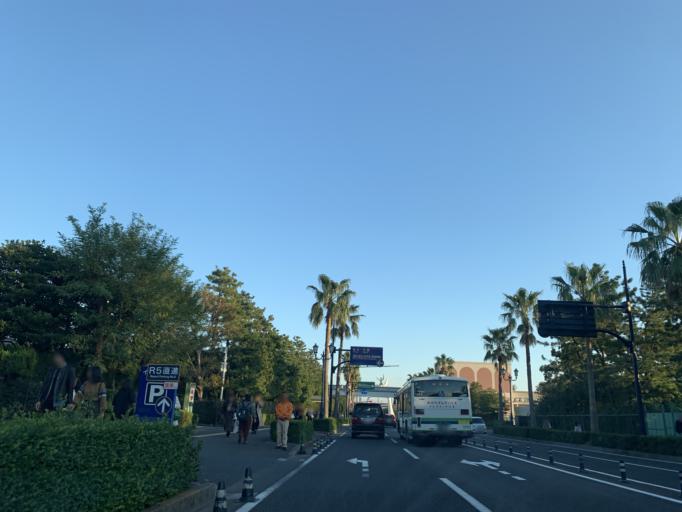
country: JP
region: Tokyo
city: Urayasu
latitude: 35.6317
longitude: 139.8880
